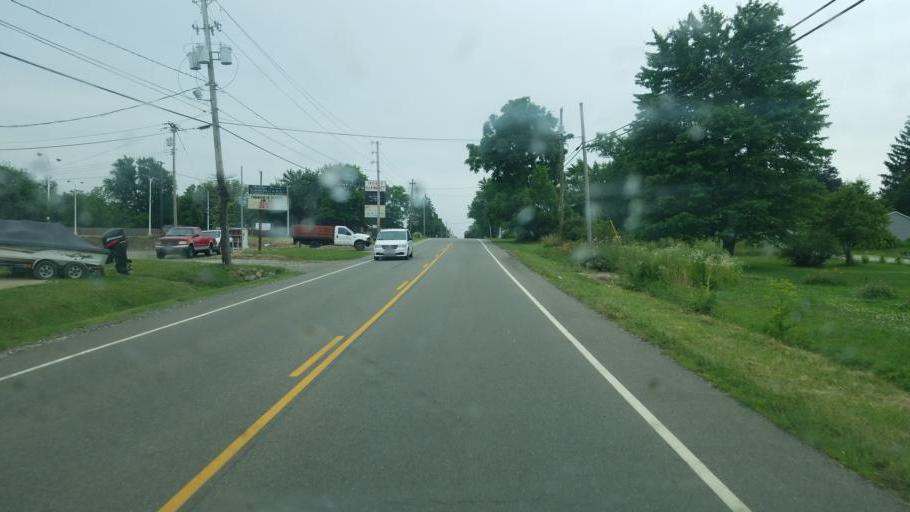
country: US
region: Ohio
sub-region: Summit County
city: Manchester
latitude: 40.9577
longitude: -81.5665
